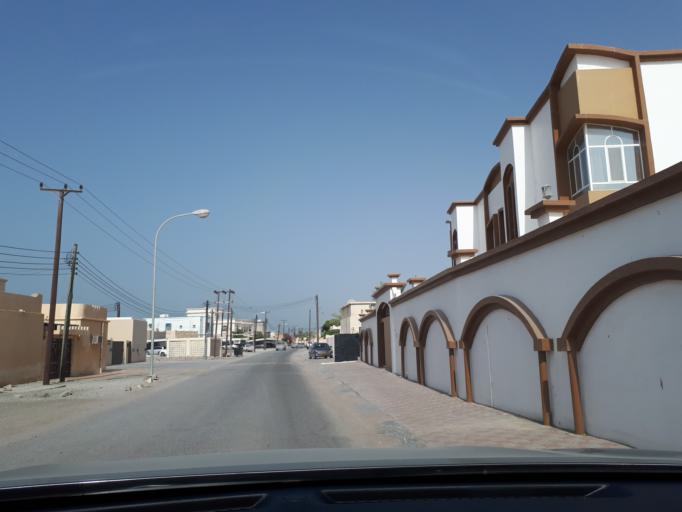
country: OM
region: Al Batinah
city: Barka'
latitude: 23.7060
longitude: 57.9238
